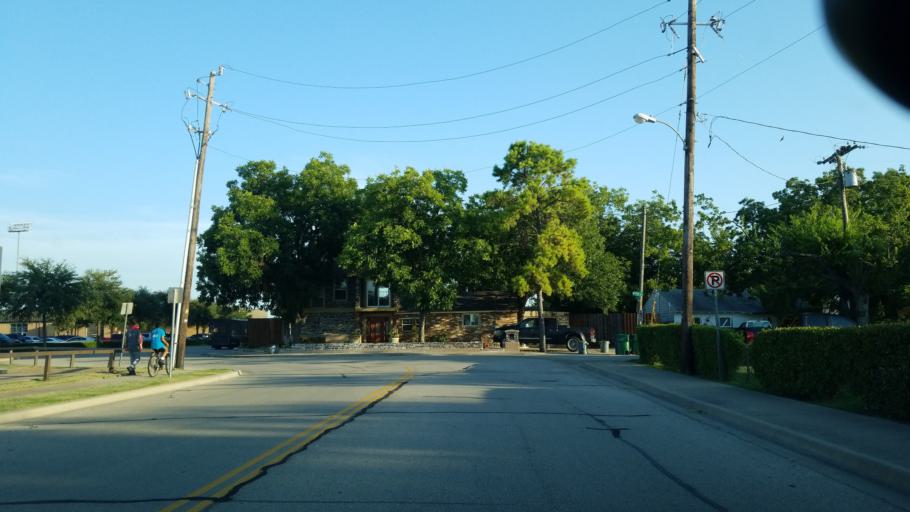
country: US
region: Texas
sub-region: Dallas County
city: Carrollton
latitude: 32.9483
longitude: -96.8934
